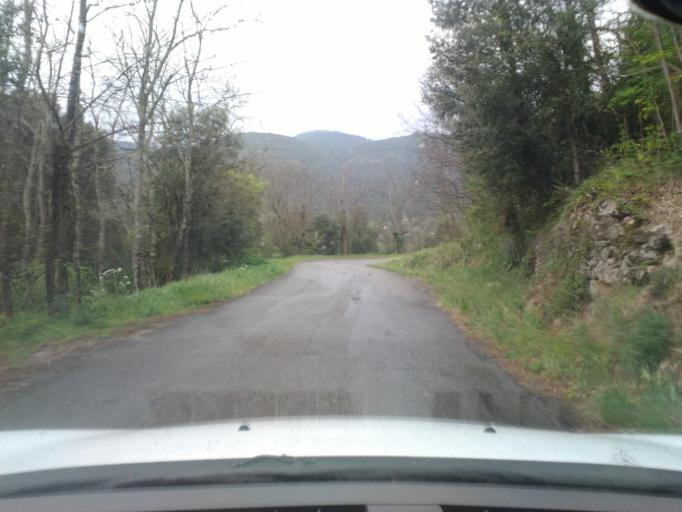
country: FR
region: Languedoc-Roussillon
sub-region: Departement du Gard
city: Valleraugue
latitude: 44.0393
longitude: 3.6755
